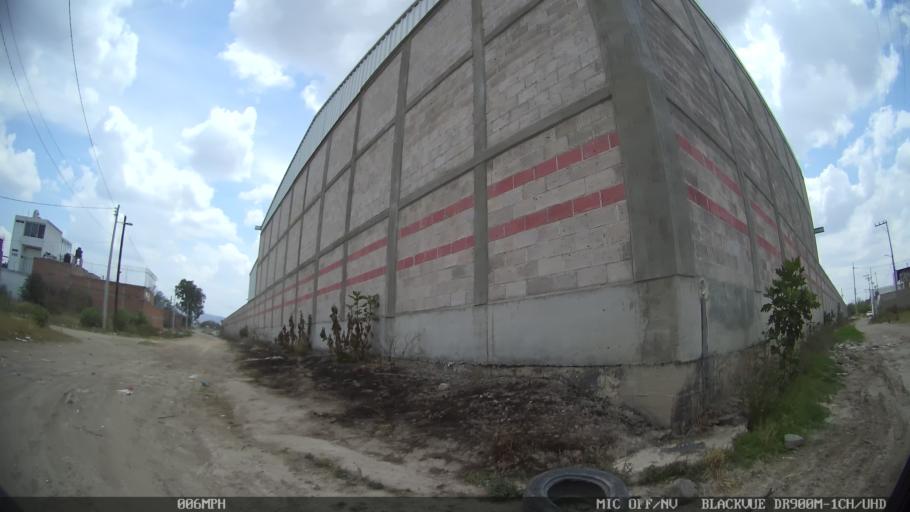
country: MX
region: Jalisco
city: Tonala
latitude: 20.6728
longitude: -103.2302
